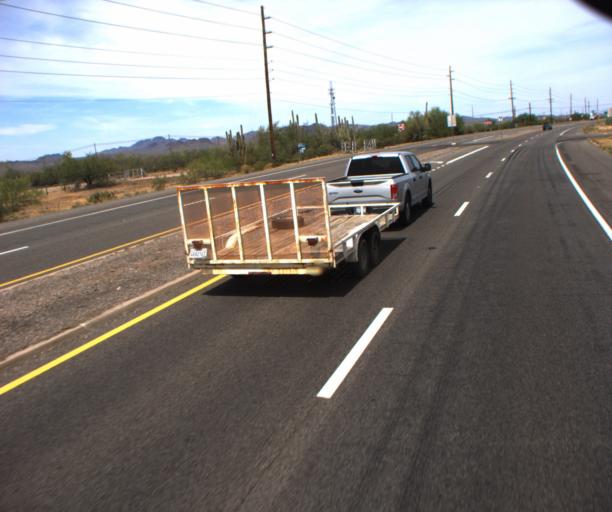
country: US
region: Arizona
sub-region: Maricopa County
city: Wickenburg
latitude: 33.8528
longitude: -112.6214
